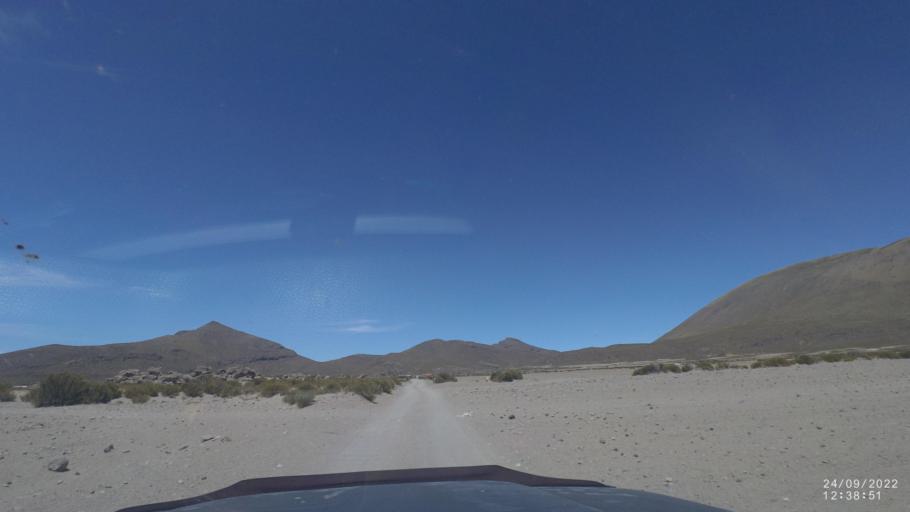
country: BO
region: Potosi
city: Colchani
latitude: -19.7916
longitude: -67.5823
